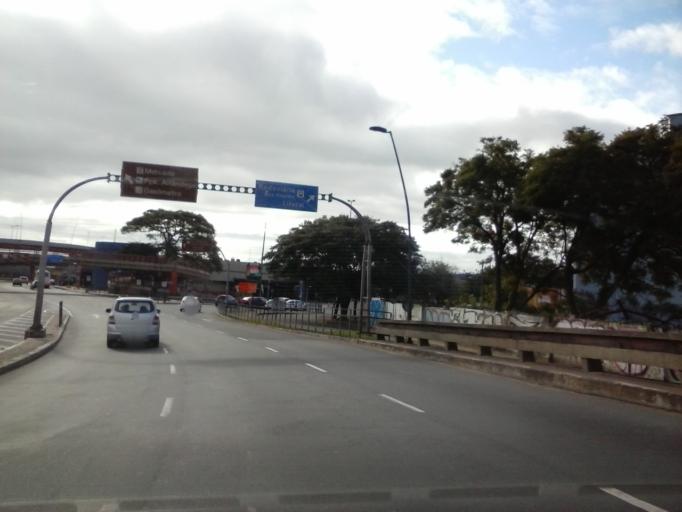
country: BR
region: Rio Grande do Sul
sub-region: Porto Alegre
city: Porto Alegre
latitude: -30.0252
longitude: -51.2189
